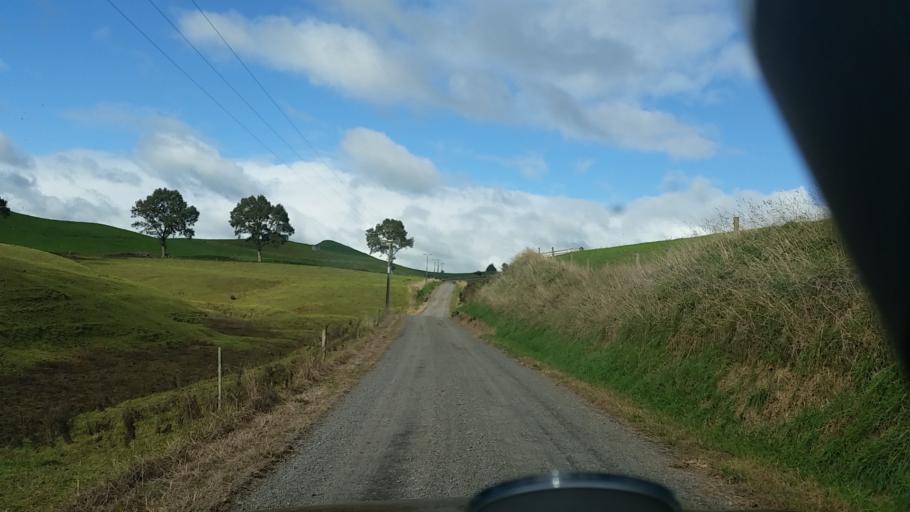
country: NZ
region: Waikato
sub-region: Matamata-Piako District
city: Matamata
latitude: -37.8180
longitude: 175.6743
